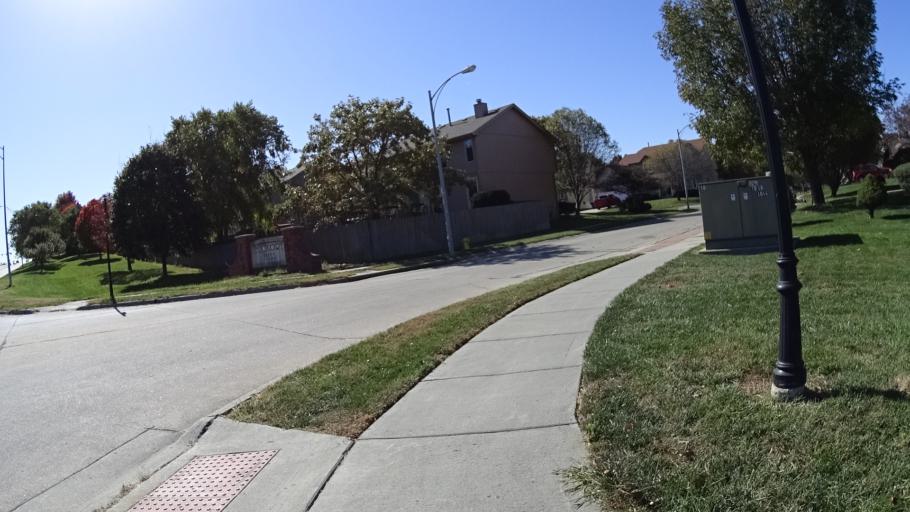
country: US
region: Nebraska
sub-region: Sarpy County
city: La Vista
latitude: 41.1682
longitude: -96.0238
